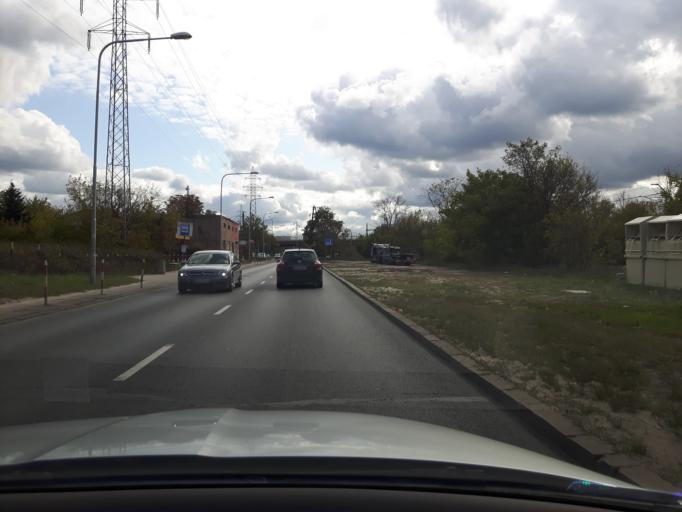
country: PL
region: Masovian Voivodeship
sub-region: Warszawa
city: Rembertow
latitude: 52.2283
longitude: 21.1451
